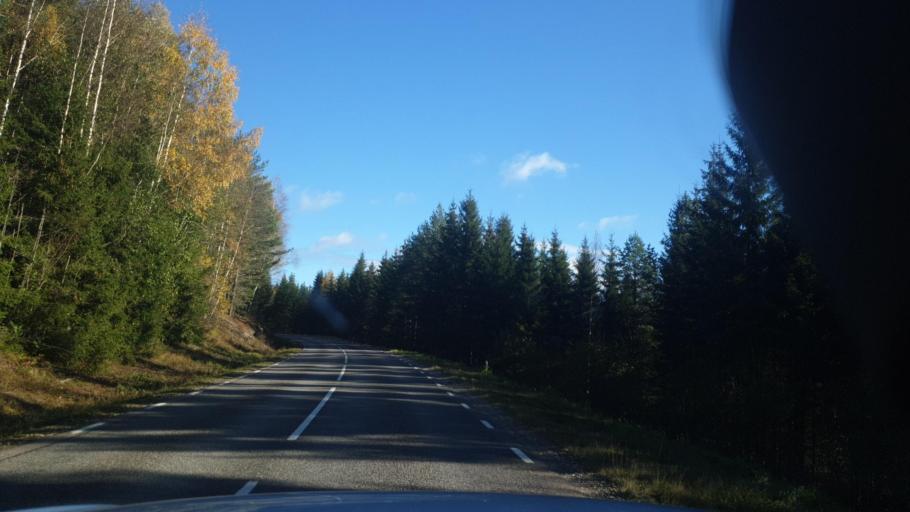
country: SE
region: Vaermland
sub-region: Arvika Kommun
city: Arvika
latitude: 59.6250
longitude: 12.8747
